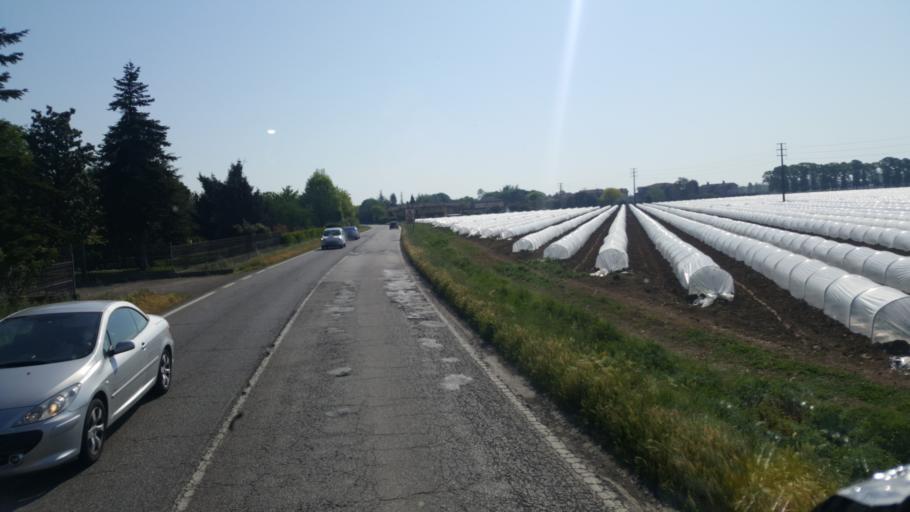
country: IT
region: Lombardy
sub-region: Provincia di Mantova
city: Montanara
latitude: 45.1516
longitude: 10.6931
